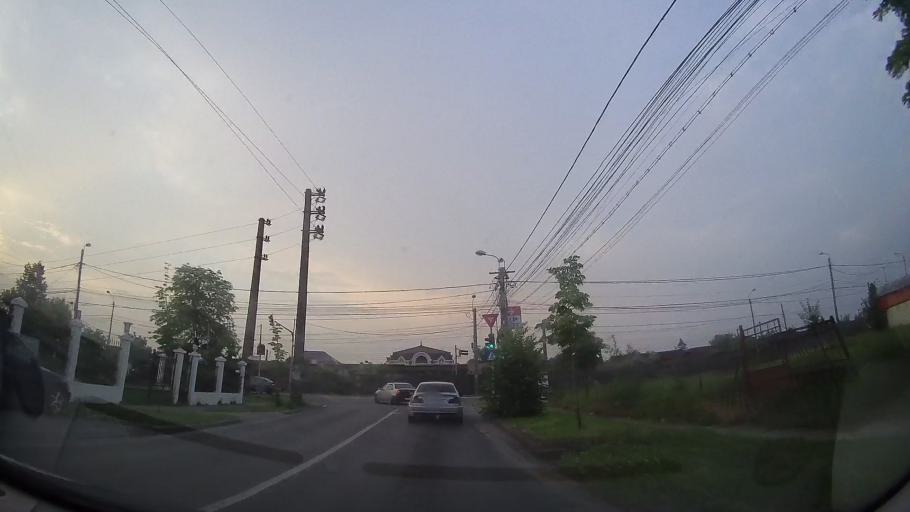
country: RO
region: Timis
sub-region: Comuna Dumbravita
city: Dumbravita
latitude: 45.7704
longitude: 21.2490
